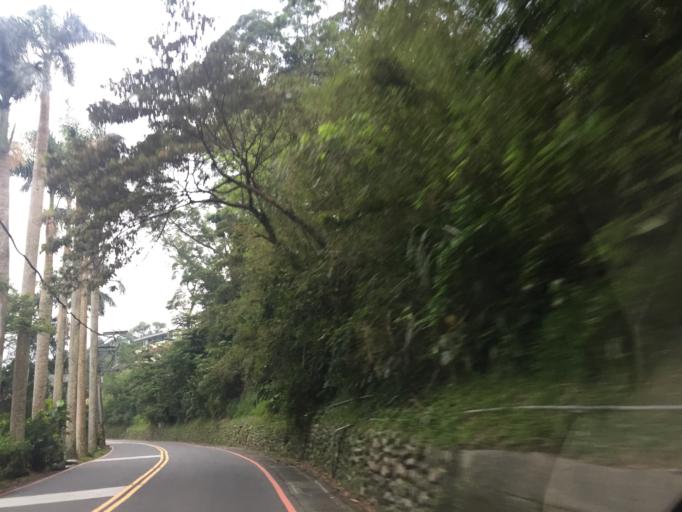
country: TW
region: Taipei
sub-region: Taipei
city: Banqiao
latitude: 24.8648
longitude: 121.5493
